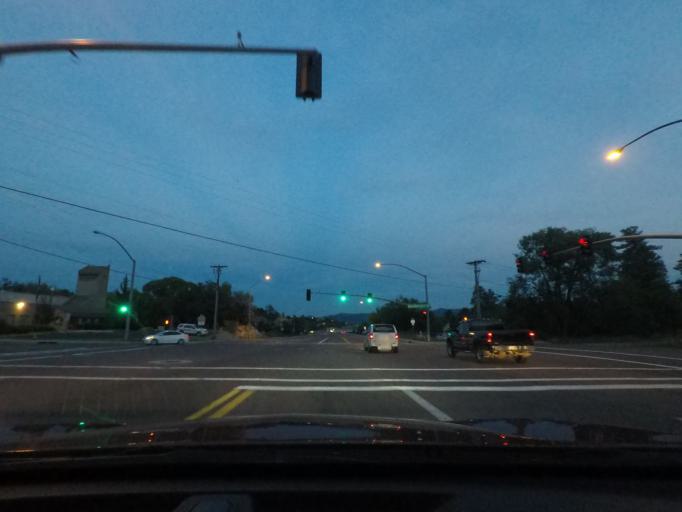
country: US
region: Arizona
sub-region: Yavapai County
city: Prescott
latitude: 34.5705
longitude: -112.5004
